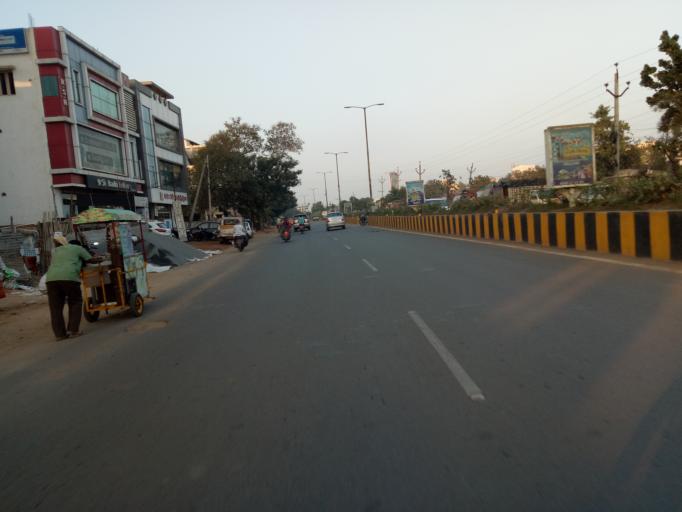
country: IN
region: Andhra Pradesh
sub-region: Nellore
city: Nellore
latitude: 14.4404
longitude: 79.9858
